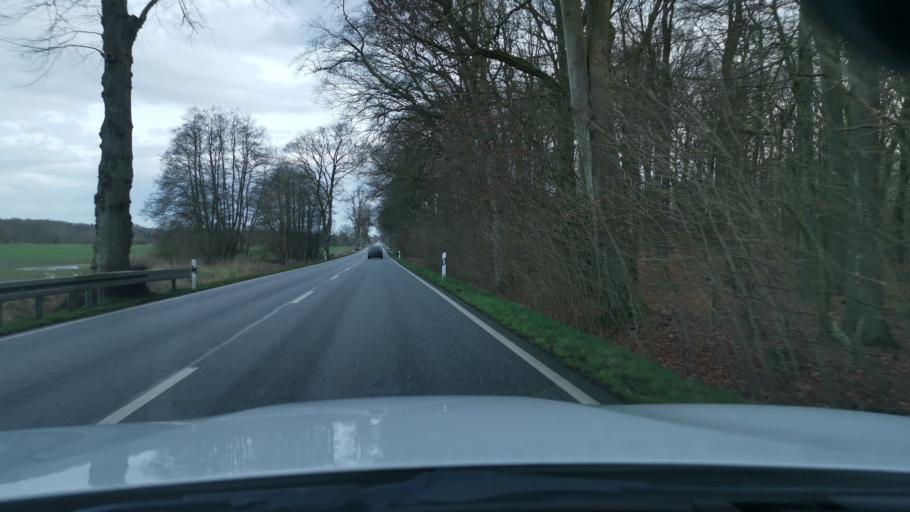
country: DE
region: Mecklenburg-Vorpommern
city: Dummerstorf
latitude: 54.0008
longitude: 12.2609
